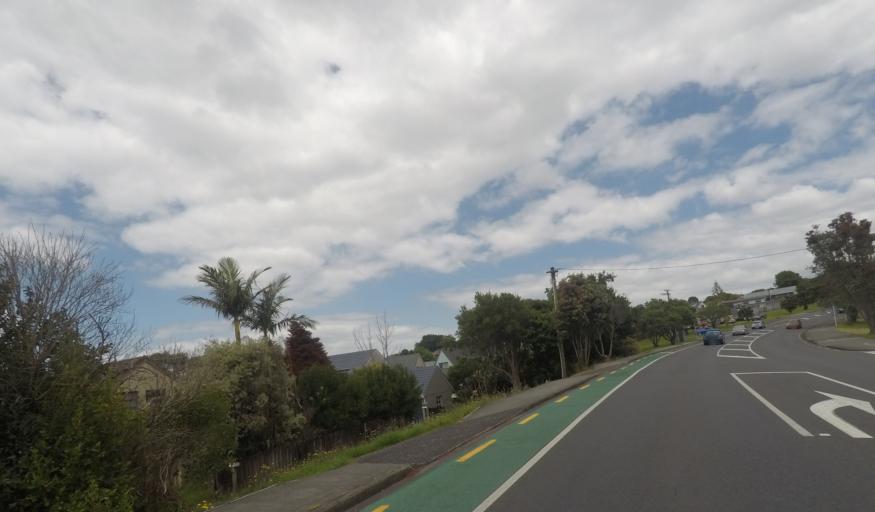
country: NZ
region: Auckland
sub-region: Auckland
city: Rosebank
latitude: -36.8276
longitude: 174.6078
